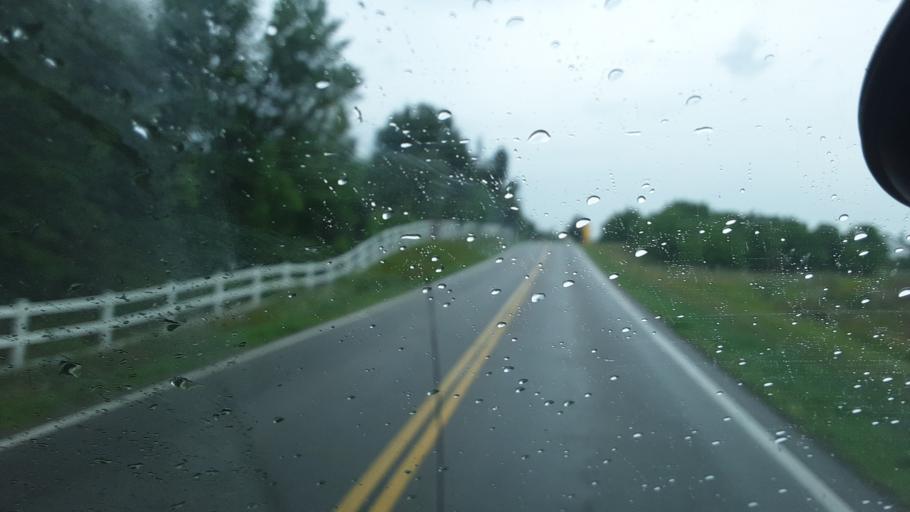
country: US
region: Ohio
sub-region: Williams County
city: Bryan
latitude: 41.5112
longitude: -84.6131
